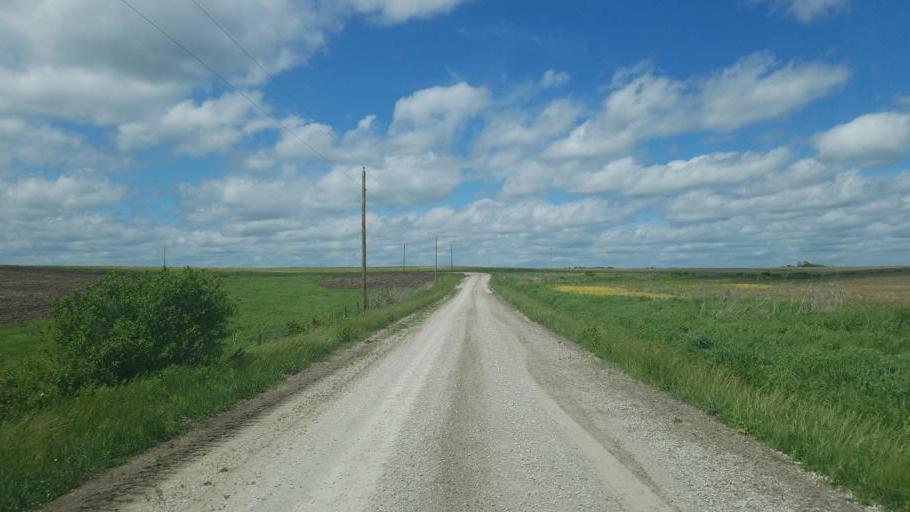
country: US
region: Iowa
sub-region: Decatur County
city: Lamoni
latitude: 40.4986
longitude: -93.9842
